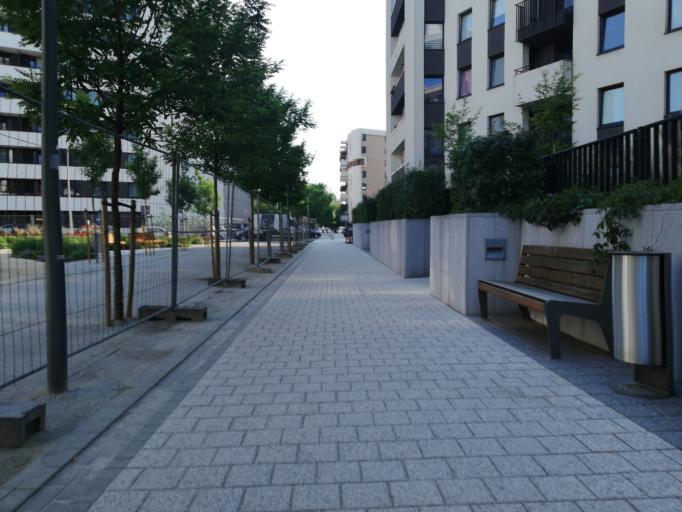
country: PL
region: Lesser Poland Voivodeship
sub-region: Krakow
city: Krakow
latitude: 50.0800
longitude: 20.0053
